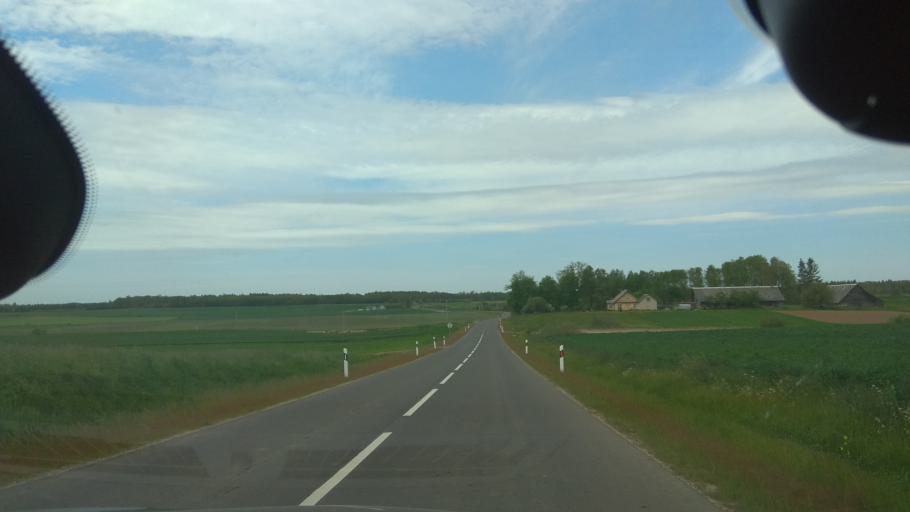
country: LT
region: Vilnius County
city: Ukmerge
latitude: 55.1064
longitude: 24.6786
